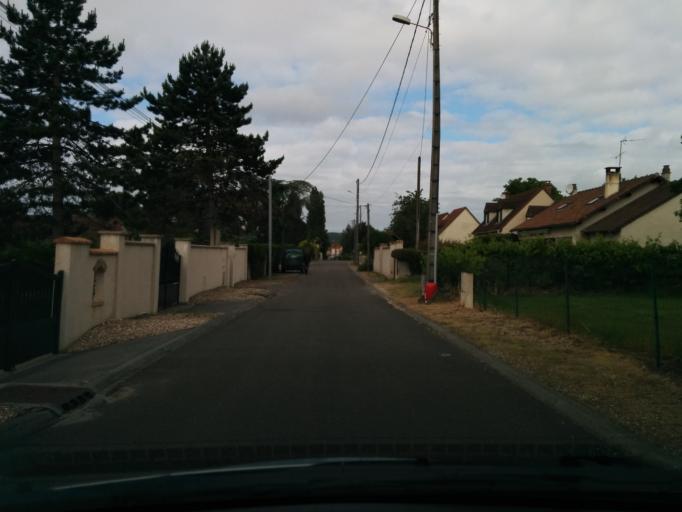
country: FR
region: Ile-de-France
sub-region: Departement des Yvelines
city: Rosny-sur-Seine
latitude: 49.0098
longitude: 1.6424
